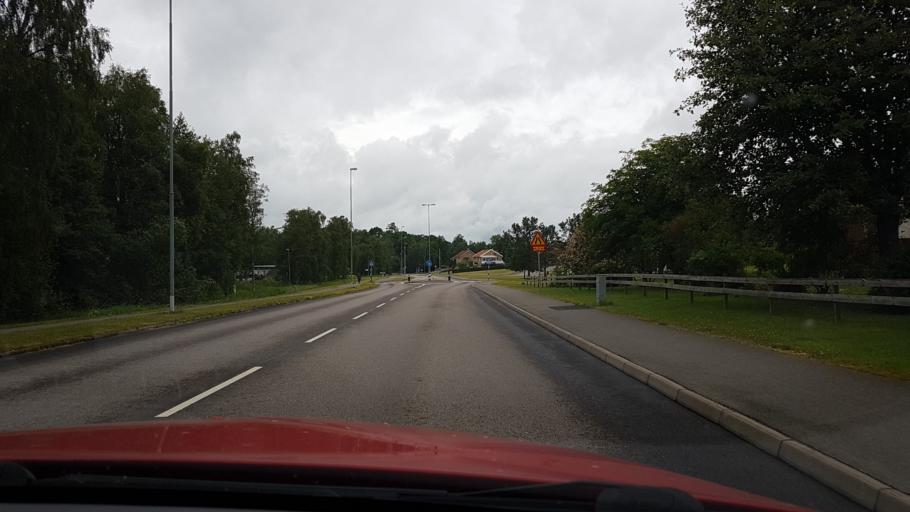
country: SE
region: Vaestra Goetaland
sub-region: Skovde Kommun
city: Skultorp
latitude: 58.3717
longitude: 13.8296
